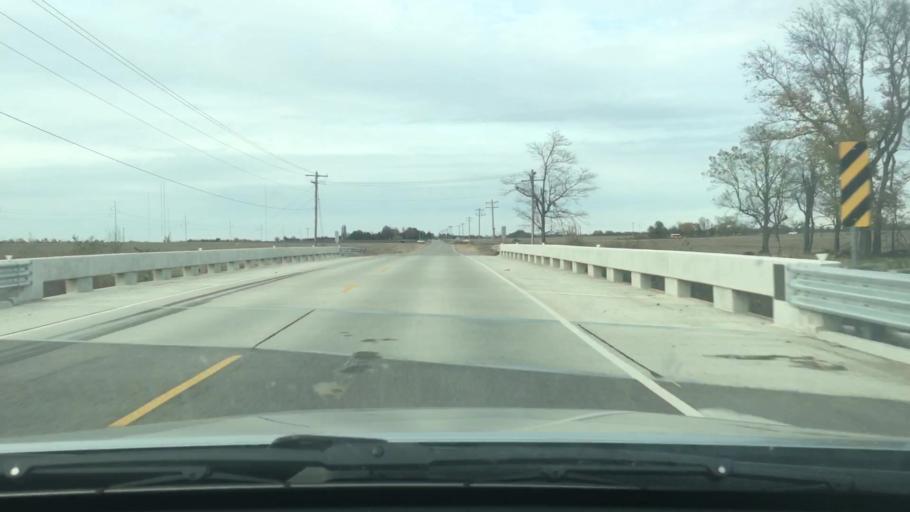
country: US
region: Kansas
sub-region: Sedgwick County
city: Maize
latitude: 37.7320
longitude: -97.4991
